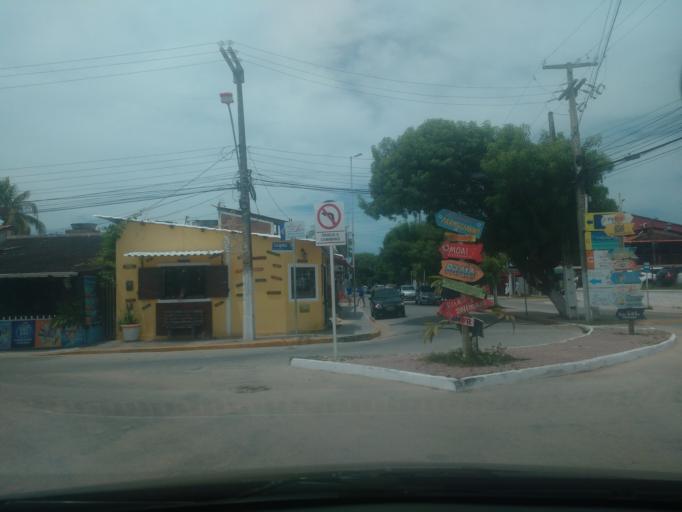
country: BR
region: Alagoas
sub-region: Marechal Deodoro
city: Marechal Deodoro
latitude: -9.7701
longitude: -35.8415
